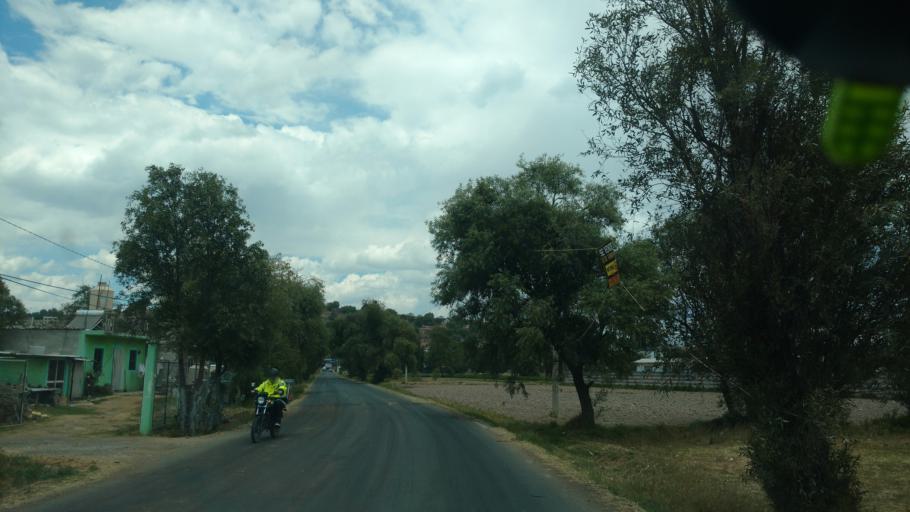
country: MX
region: Tlaxcala
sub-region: Tetlatlahuca
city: Tetlatlahuca
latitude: 19.2267
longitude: -98.2939
